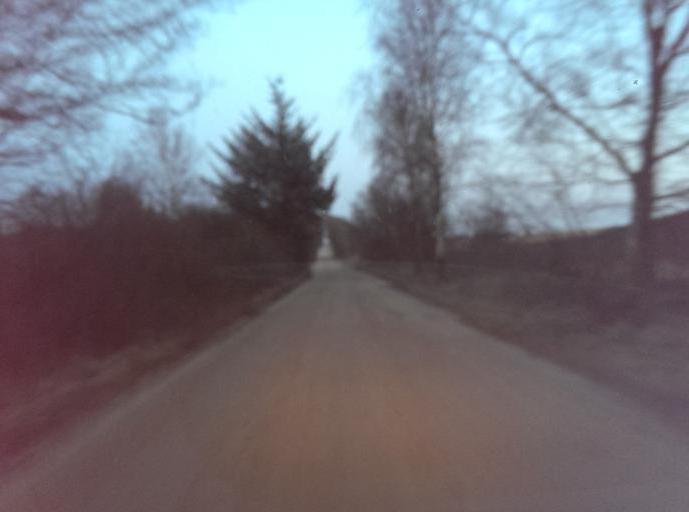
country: DK
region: South Denmark
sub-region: Varde Kommune
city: Oksbol
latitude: 55.5537
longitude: 8.3220
